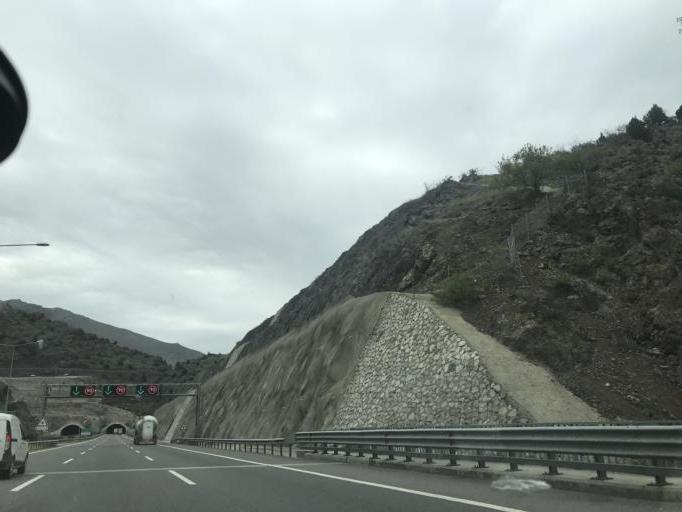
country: TR
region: Nigde
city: Ciftehan
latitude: 37.5555
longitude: 34.7695
